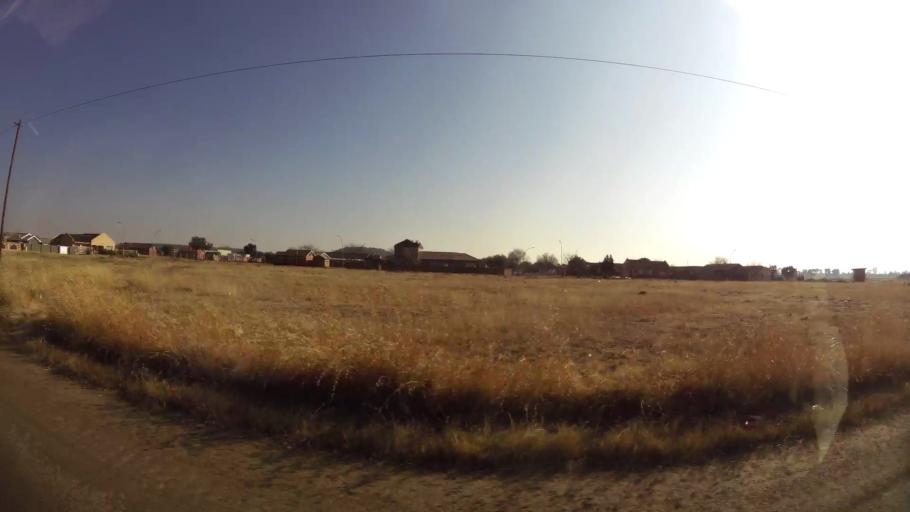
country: ZA
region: Orange Free State
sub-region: Mangaung Metropolitan Municipality
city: Bloemfontein
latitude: -29.1851
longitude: 26.1809
